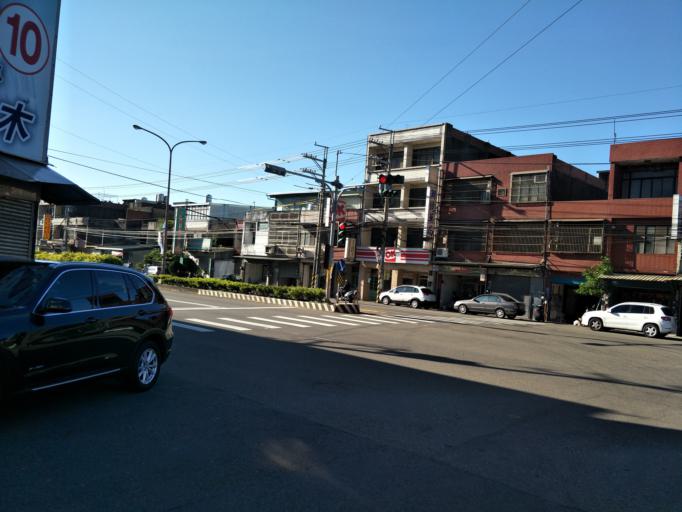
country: TW
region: Taiwan
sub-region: Hsinchu
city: Zhubei
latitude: 24.8777
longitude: 121.0524
